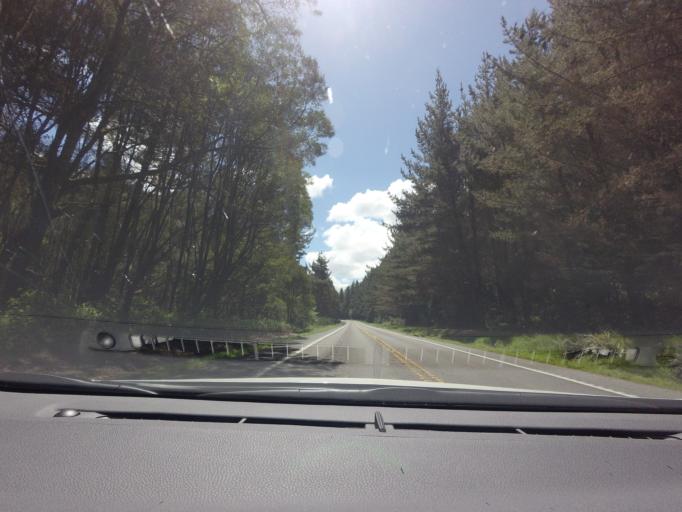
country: NZ
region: Bay of Plenty
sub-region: Rotorua District
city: Rotorua
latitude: -38.1877
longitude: 176.2576
